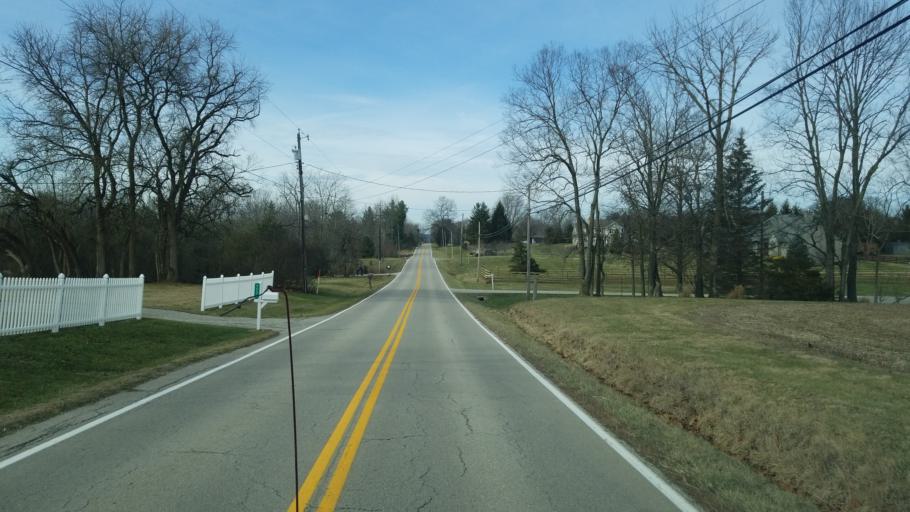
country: US
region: Ohio
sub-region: Warren County
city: Lebanon
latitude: 39.4294
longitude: -84.1493
